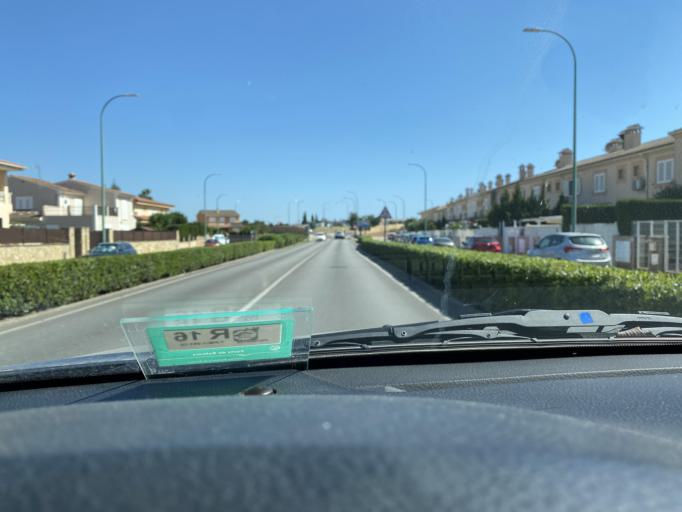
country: ES
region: Balearic Islands
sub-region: Illes Balears
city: Palma
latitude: 39.6087
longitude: 2.6853
